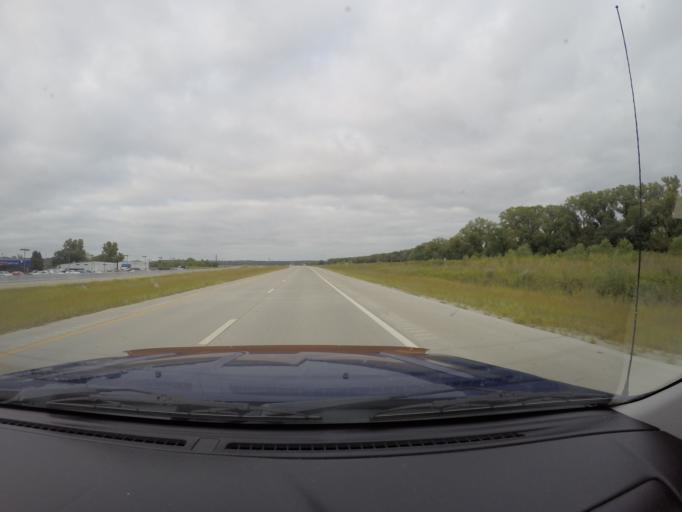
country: US
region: Kansas
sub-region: Riley County
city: Ogden
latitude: 39.1427
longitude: -96.6553
